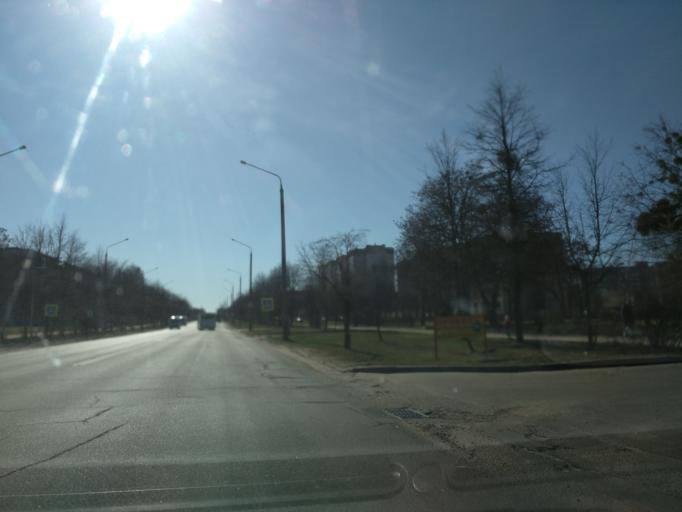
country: BY
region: Mogilev
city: Babruysk
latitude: 53.1765
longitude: 29.1929
